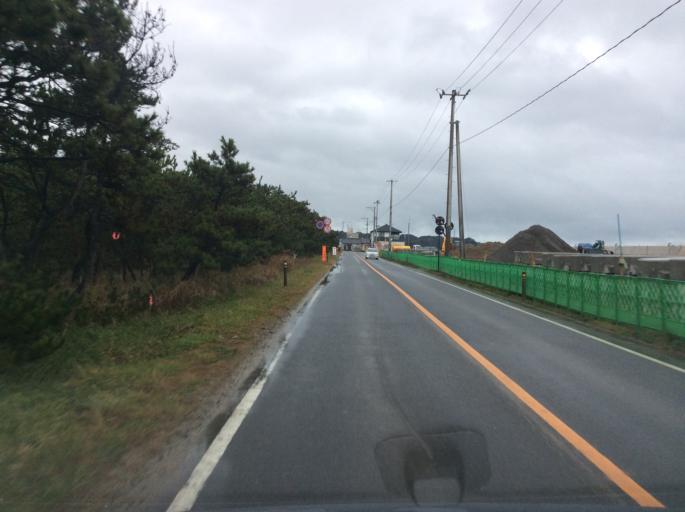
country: JP
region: Fukushima
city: Iwaki
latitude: 37.0932
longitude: 140.9841
